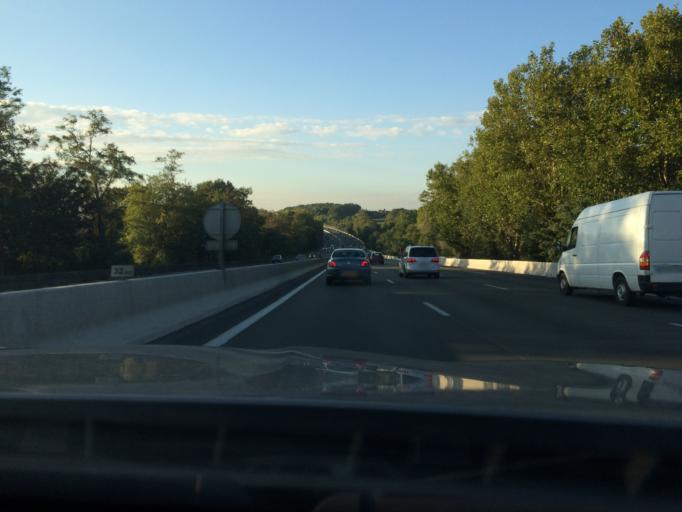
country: FR
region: Ile-de-France
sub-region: Departement de l'Essonne
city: Ormoy
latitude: 48.5740
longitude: 2.4669
